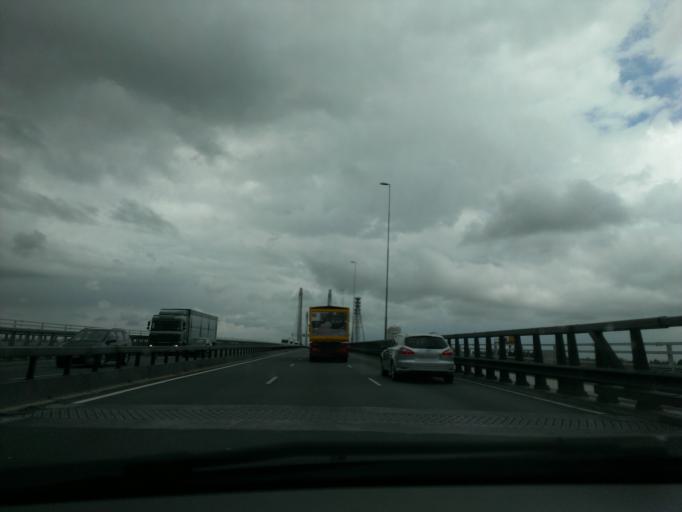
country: NL
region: Gelderland
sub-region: Gemeente Overbetuwe
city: Andelst
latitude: 51.8801
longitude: 5.7352
